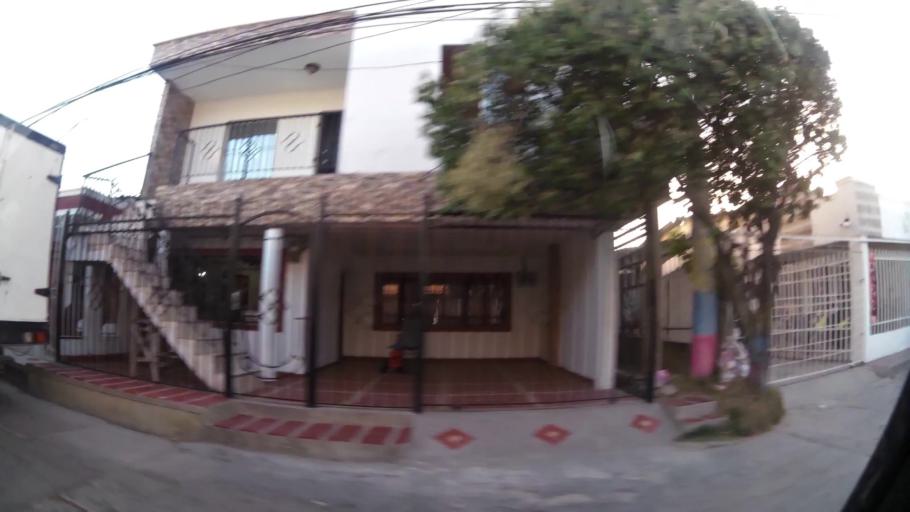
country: CO
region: Atlantico
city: Soledad
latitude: 10.9303
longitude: -74.7771
